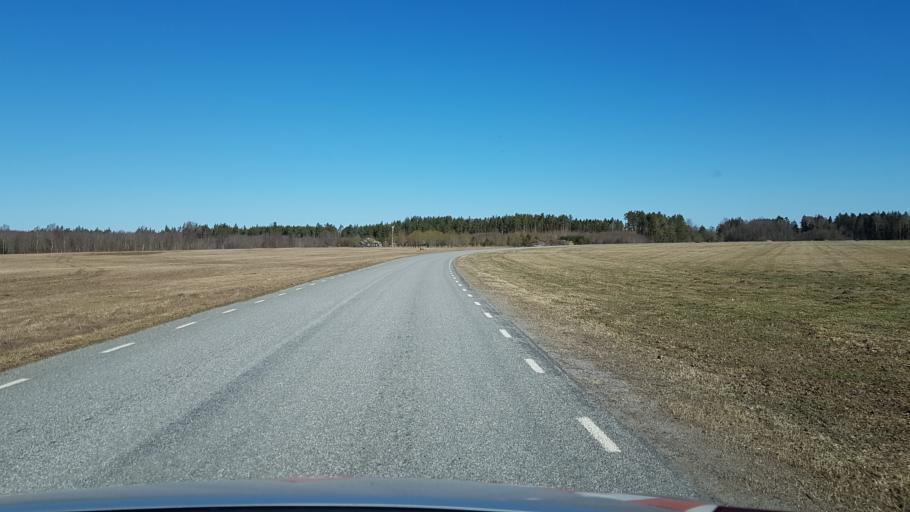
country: EE
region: Laeaene-Virumaa
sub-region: Haljala vald
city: Haljala
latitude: 59.4674
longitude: 26.2422
